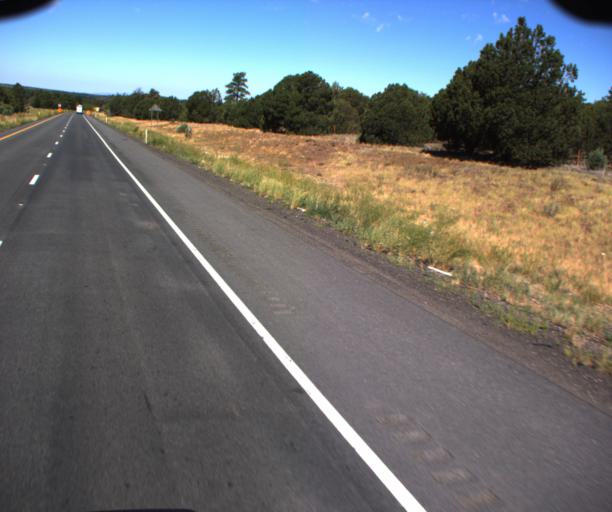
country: US
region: Arizona
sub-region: Coconino County
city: Williams
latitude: 35.2225
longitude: -112.2625
